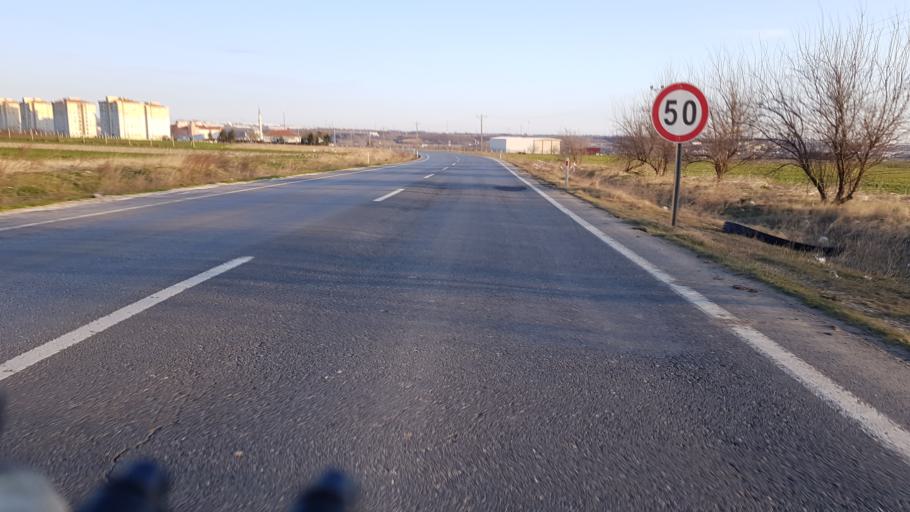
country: TR
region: Tekirdag
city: Velimese
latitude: 41.2565
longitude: 27.8613
